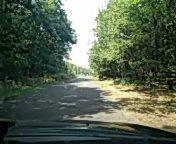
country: HU
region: Hajdu-Bihar
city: Hajdusamson
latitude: 47.5257
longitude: 21.7343
